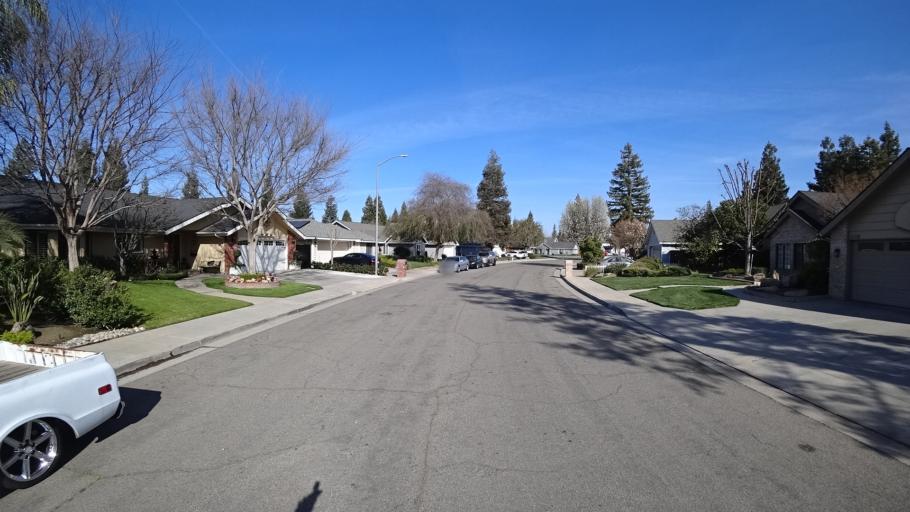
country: US
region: California
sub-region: Fresno County
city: Clovis
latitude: 36.8799
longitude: -119.7754
